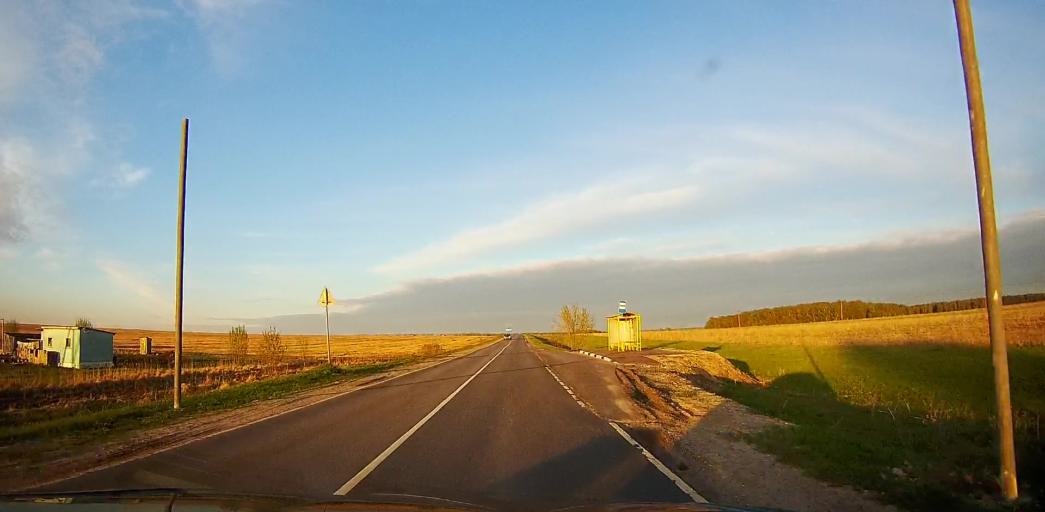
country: RU
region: Moskovskaya
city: Peski
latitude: 55.2102
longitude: 38.6781
